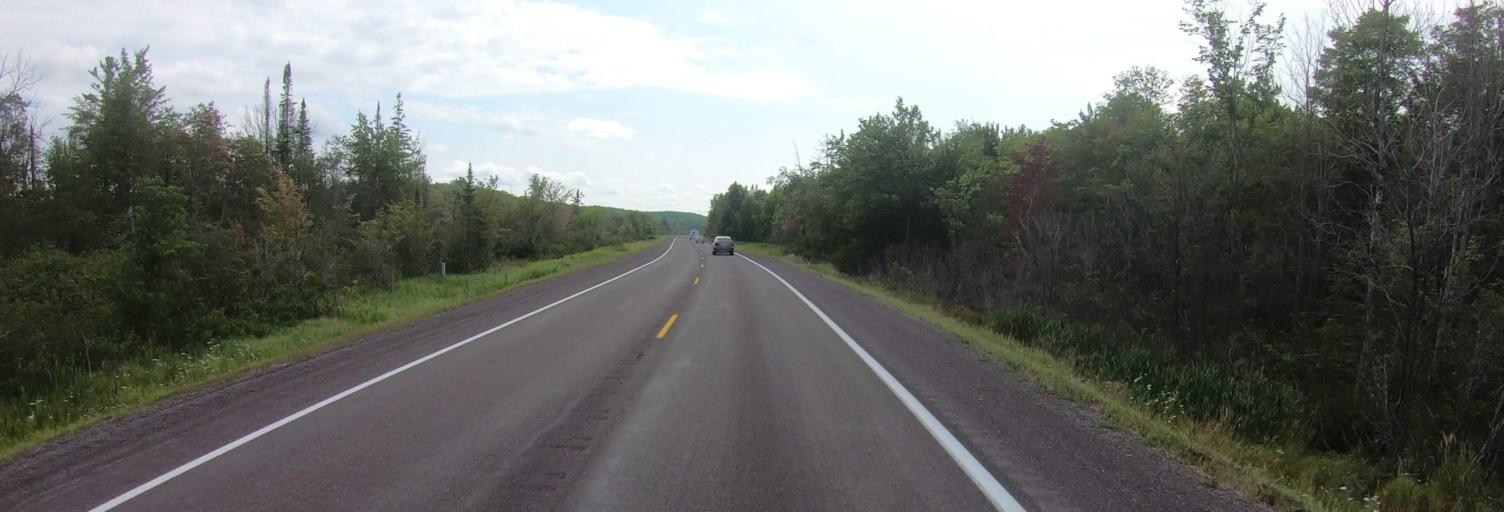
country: US
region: Michigan
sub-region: Houghton County
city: Hancock
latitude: 46.9341
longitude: -88.8003
